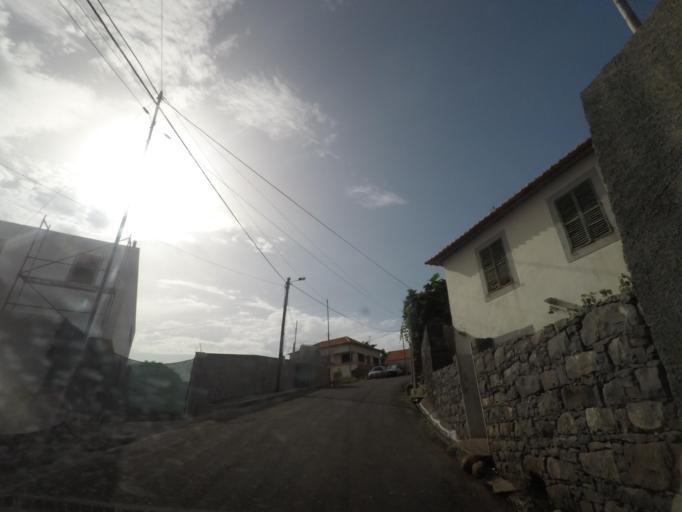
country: PT
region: Madeira
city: Ponta do Sol
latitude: 32.6961
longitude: -17.1176
